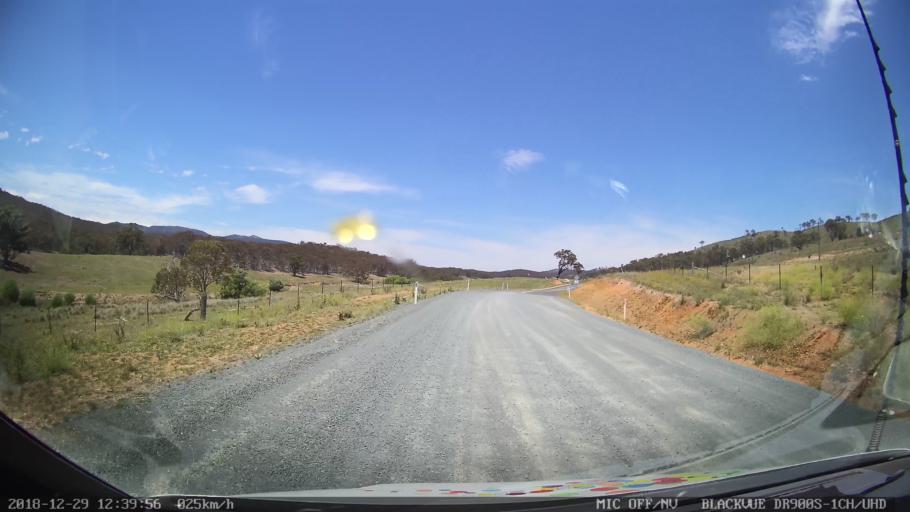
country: AU
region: Australian Capital Territory
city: Macarthur
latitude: -35.5982
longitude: 149.2265
